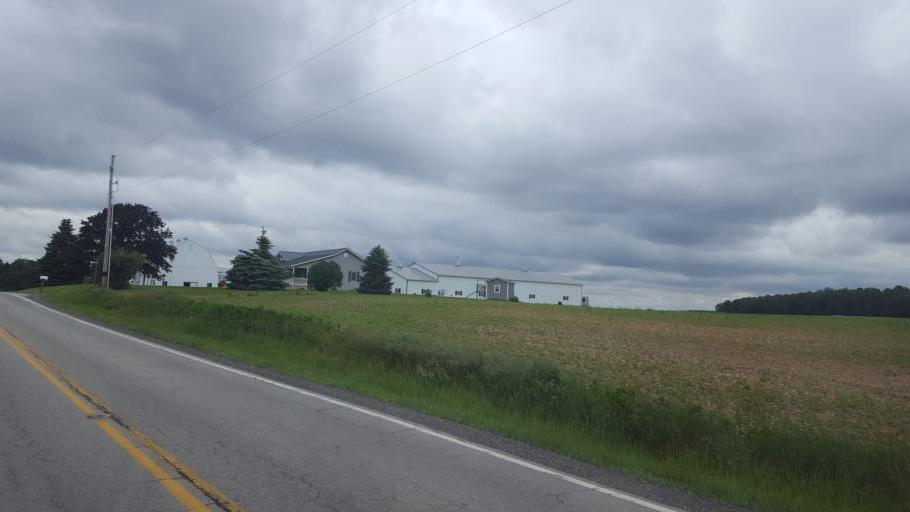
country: US
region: Ohio
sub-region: Crawford County
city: Bucyrus
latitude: 40.7620
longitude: -82.9167
